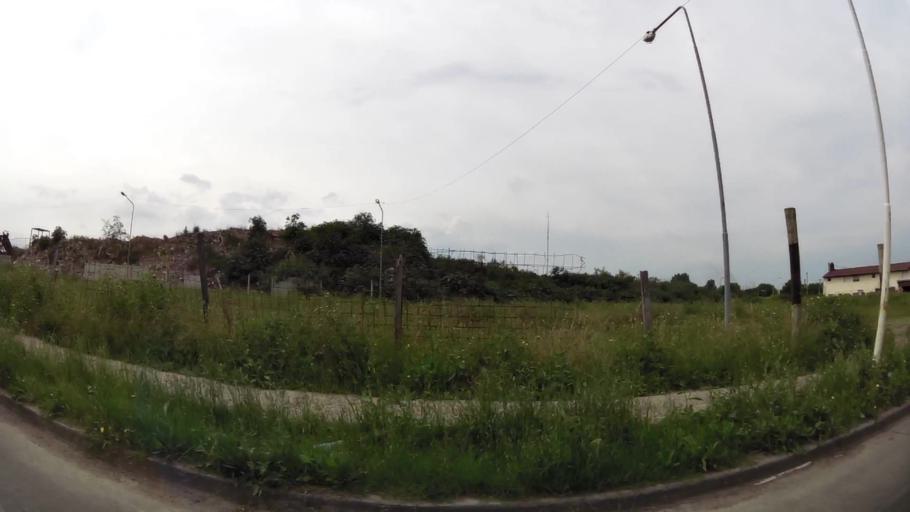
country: AR
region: Buenos Aires
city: San Justo
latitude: -34.6966
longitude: -58.5189
